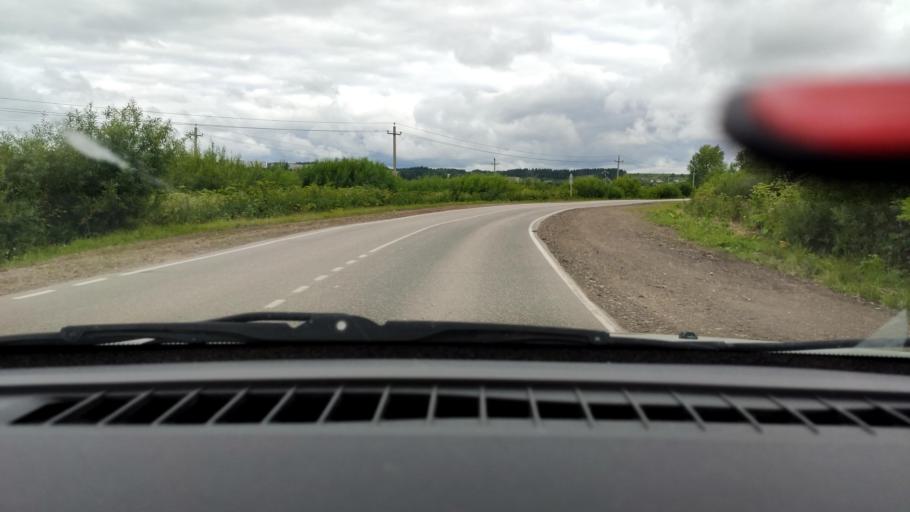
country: RU
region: Perm
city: Chaykovskaya
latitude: 58.0947
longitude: 55.5958
